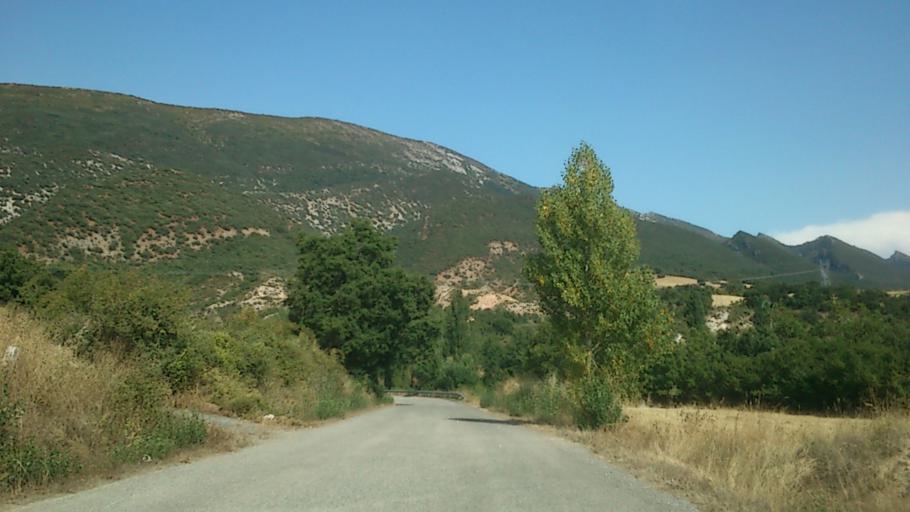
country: ES
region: Castille and Leon
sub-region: Provincia de Burgos
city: Frias
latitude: 42.8193
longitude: -3.2340
